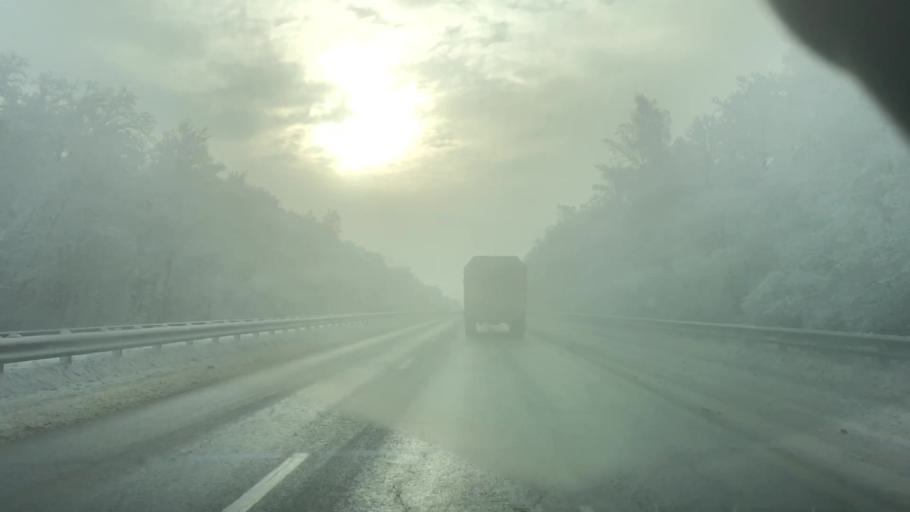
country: RU
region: Tula
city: Venev
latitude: 54.3696
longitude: 38.1547
